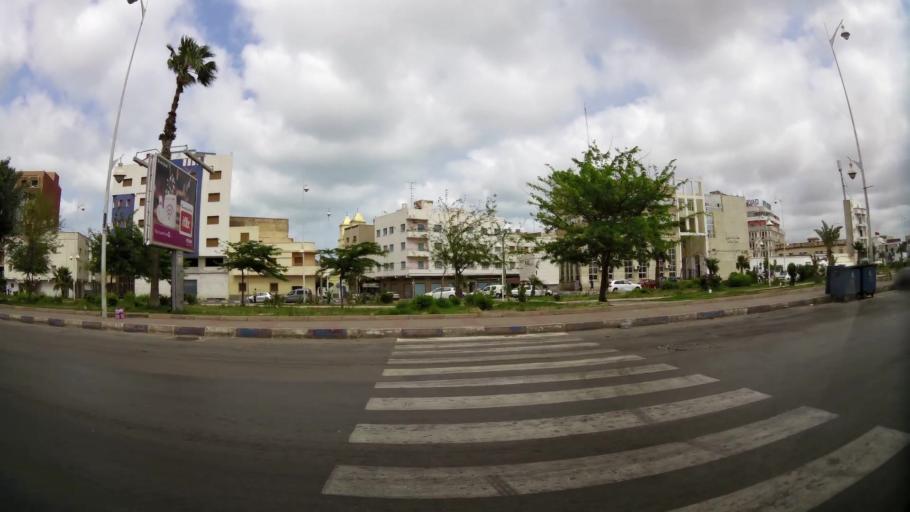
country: MA
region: Oriental
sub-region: Nador
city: Nador
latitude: 35.1807
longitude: -2.9285
